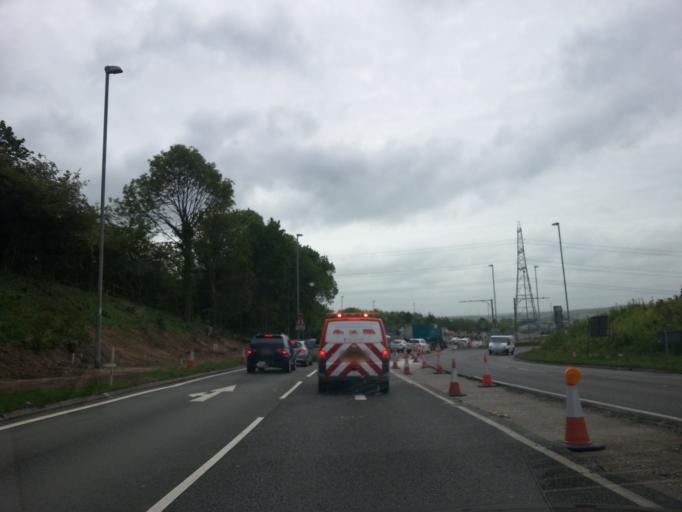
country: GB
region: England
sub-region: Borough of Halton
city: Halton
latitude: 53.3145
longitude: -2.7079
